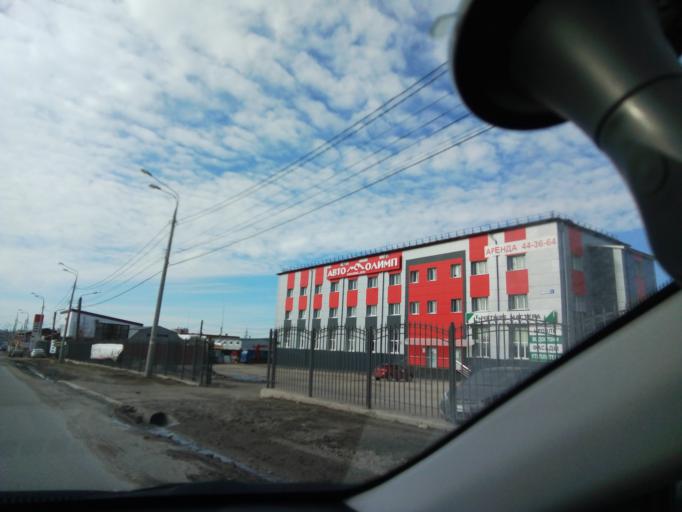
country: RU
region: Chuvashia
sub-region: Cheboksarskiy Rayon
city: Cheboksary
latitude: 56.1052
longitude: 47.2516
